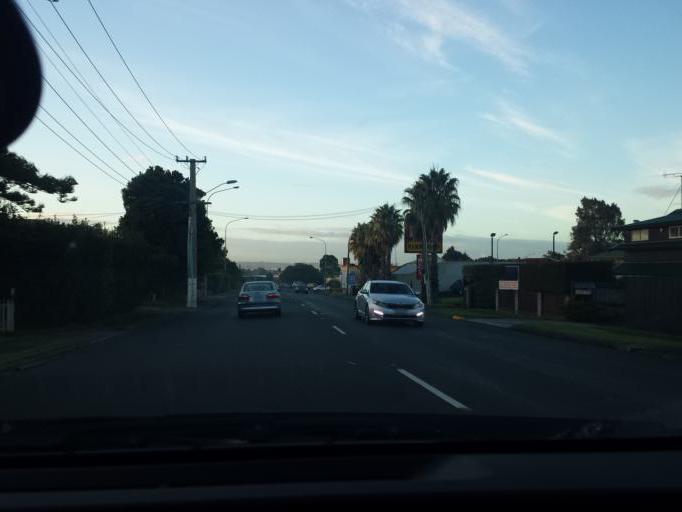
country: NZ
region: Auckland
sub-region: Auckland
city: Tamaki
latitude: -36.8952
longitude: 174.8403
